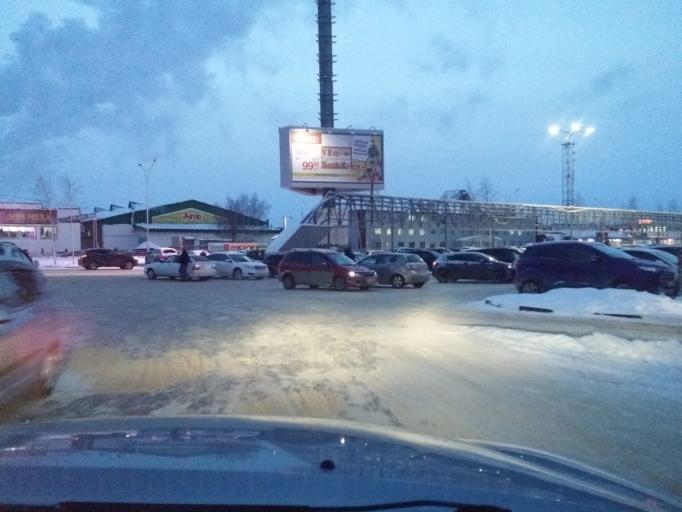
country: RU
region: Khanty-Mansiyskiy Avtonomnyy Okrug
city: Nizhnevartovsk
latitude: 60.9399
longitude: 76.5481
